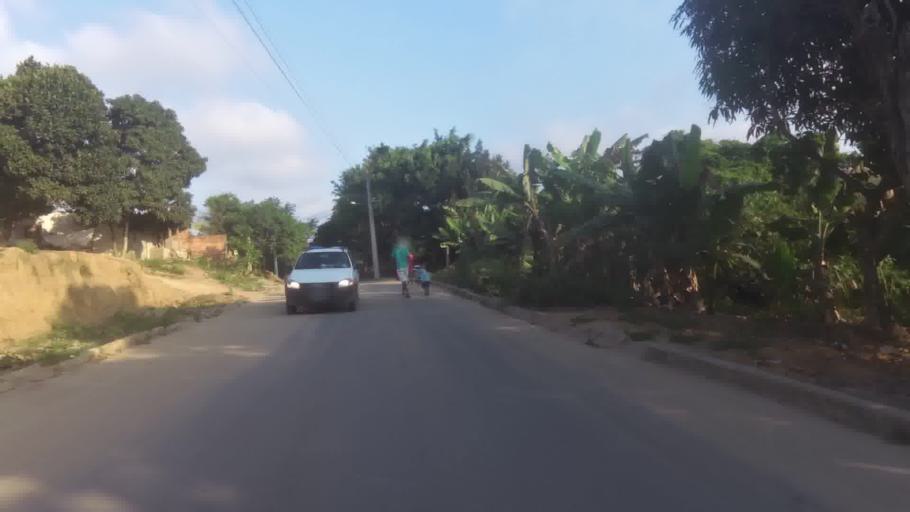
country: BR
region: Espirito Santo
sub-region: Itapemirim
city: Itapemirim
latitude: -21.0161
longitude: -40.8302
